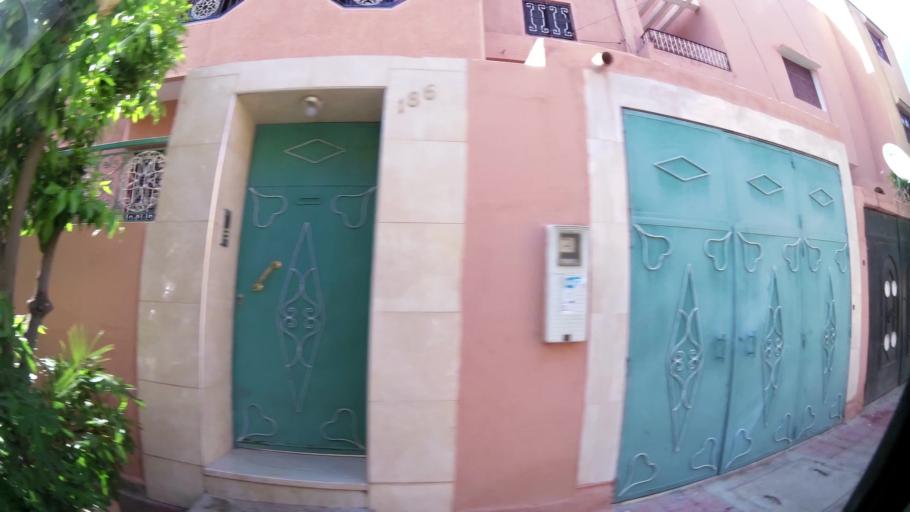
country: MA
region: Marrakech-Tensift-Al Haouz
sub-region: Marrakech
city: Marrakesh
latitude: 31.6528
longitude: -8.0066
